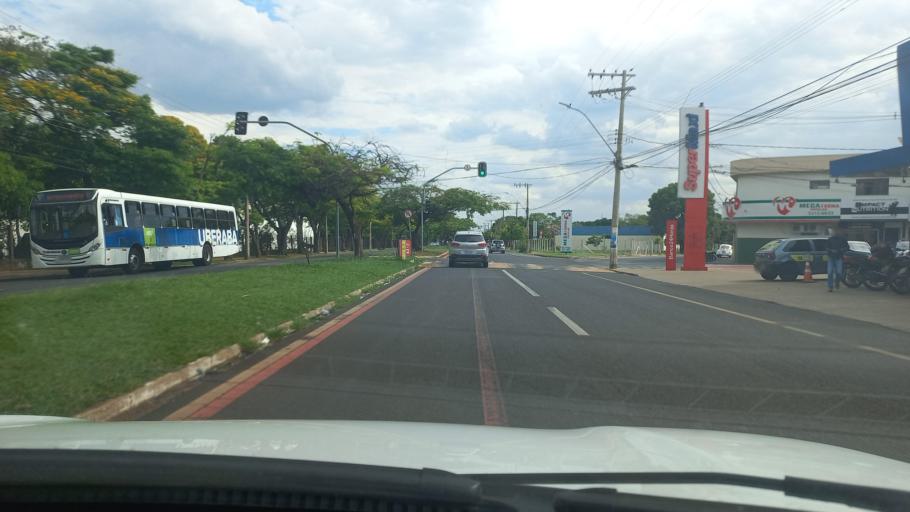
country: BR
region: Minas Gerais
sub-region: Uberaba
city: Uberaba
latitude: -19.7557
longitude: -47.9650
